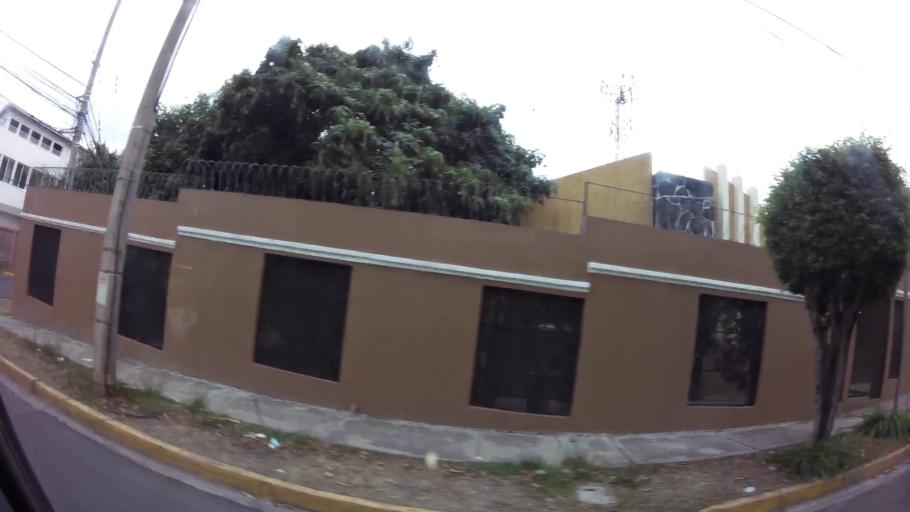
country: HN
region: Francisco Morazan
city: Tegucigalpa
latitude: 14.0960
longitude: -87.1920
